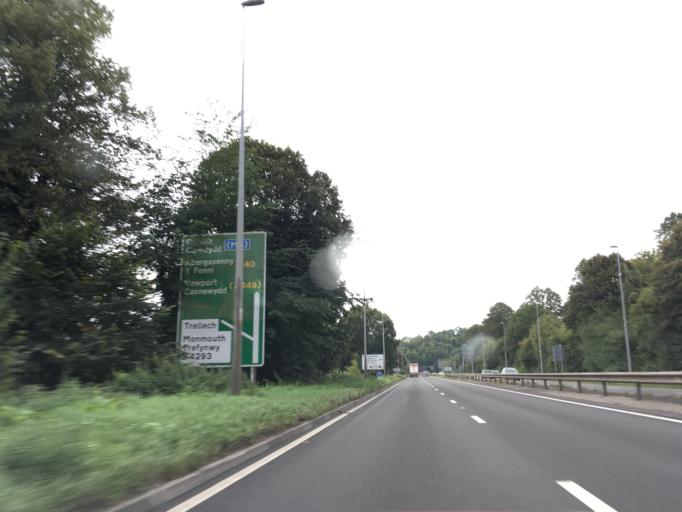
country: GB
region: Wales
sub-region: Monmouthshire
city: Monmouth
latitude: 51.8095
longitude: -2.7123
